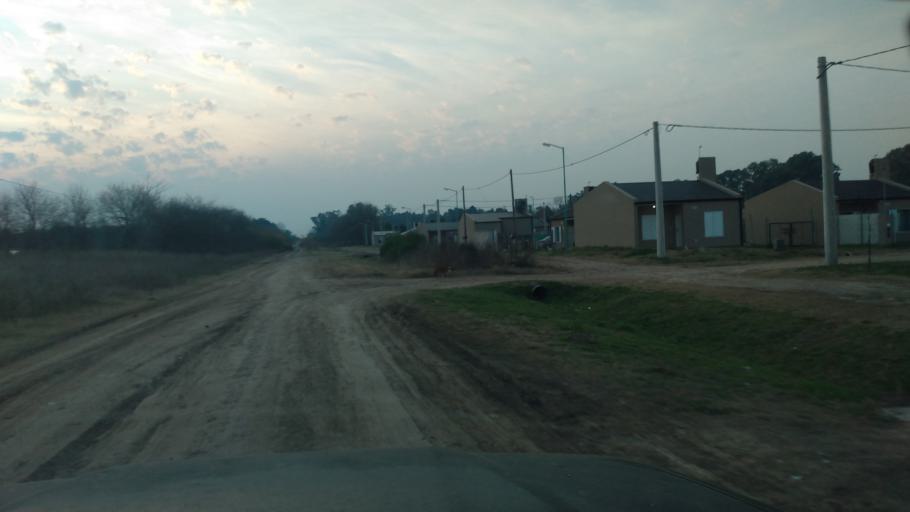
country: AR
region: Buenos Aires
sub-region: Partido de Lujan
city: Lujan
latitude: -34.5546
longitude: -59.1380
